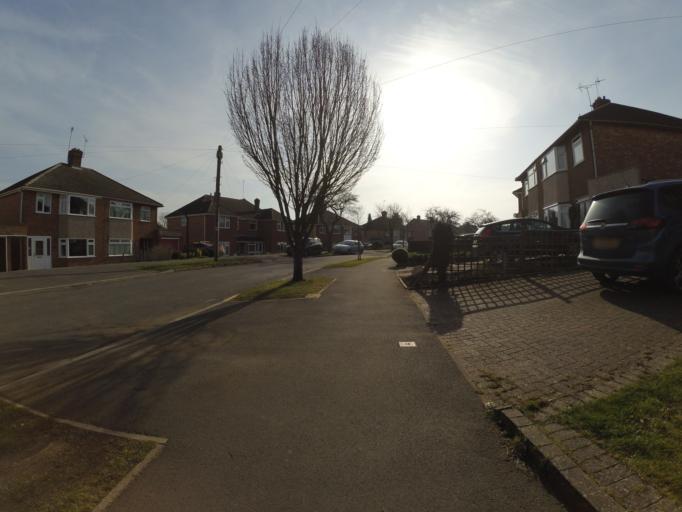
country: GB
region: England
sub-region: Warwickshire
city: Rugby
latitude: 52.3684
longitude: -1.2330
